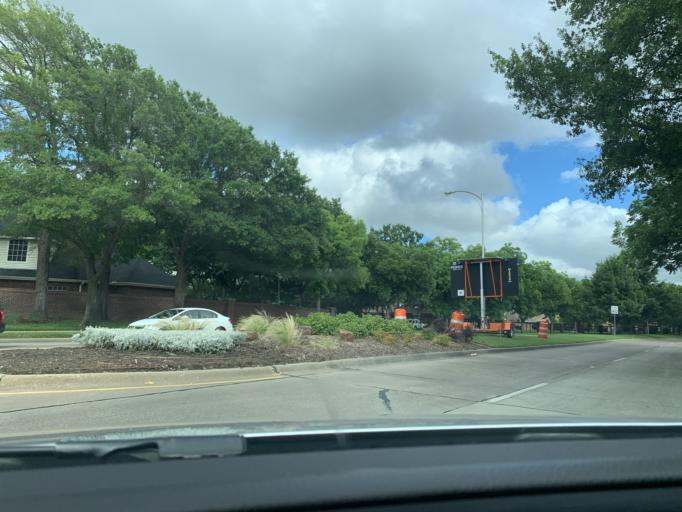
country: US
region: Texas
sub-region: Dallas County
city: Grand Prairie
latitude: 32.6687
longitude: -97.0034
